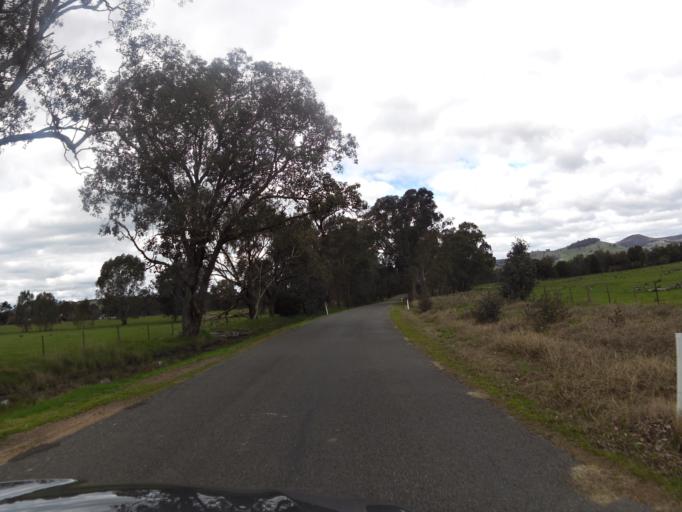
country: AU
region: Victoria
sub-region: Benalla
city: Benalla
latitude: -36.6575
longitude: 145.9099
